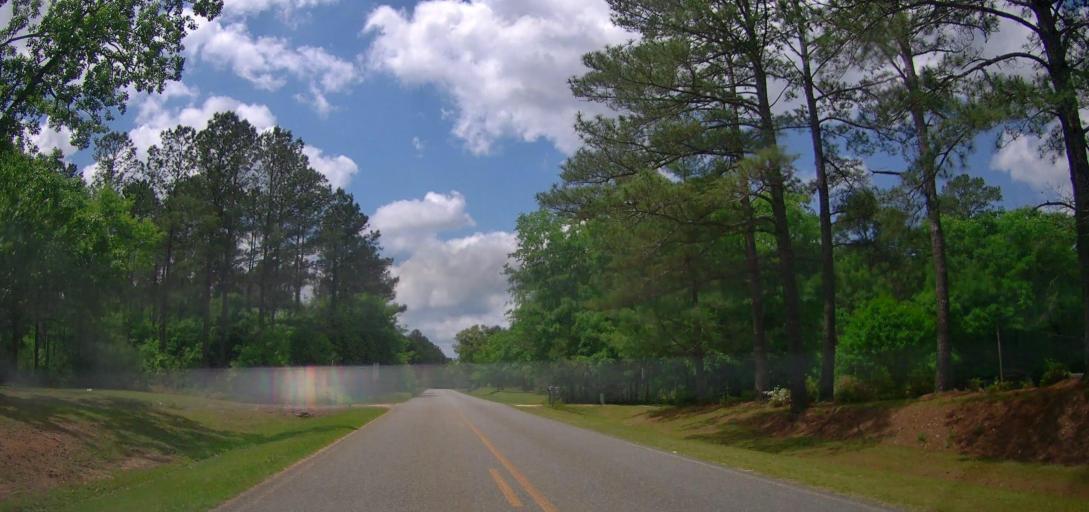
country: US
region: Georgia
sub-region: Laurens County
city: Dublin
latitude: 32.5954
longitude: -83.0190
